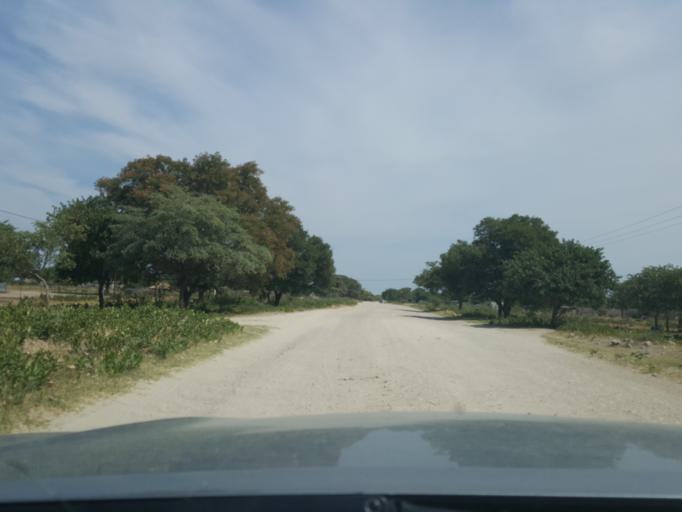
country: BW
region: North West
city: Shakawe
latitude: -18.3145
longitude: 21.9005
